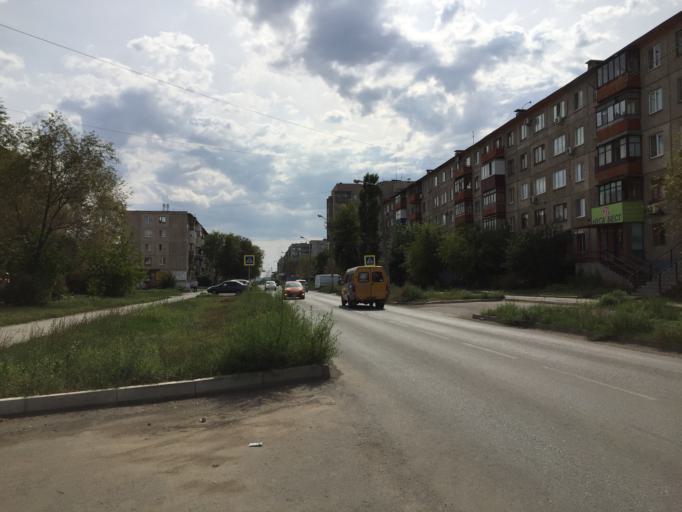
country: RU
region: Orenburg
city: Novotroitsk
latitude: 51.1875
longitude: 58.2797
